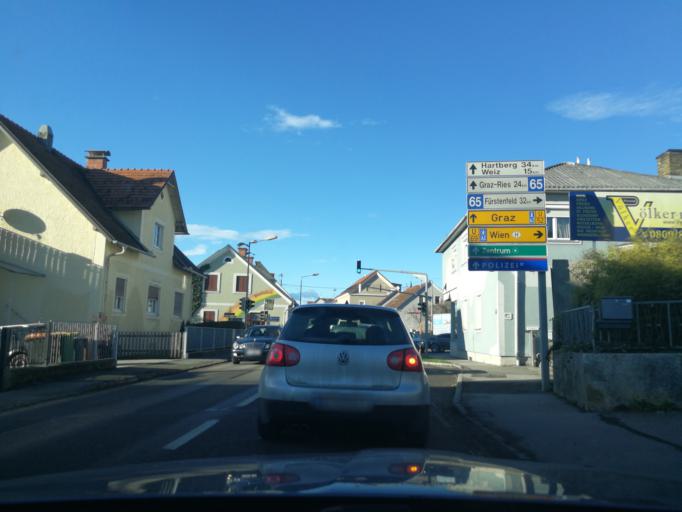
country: AT
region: Styria
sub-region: Politischer Bezirk Weiz
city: Gleisdorf
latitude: 47.1012
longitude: 15.7154
